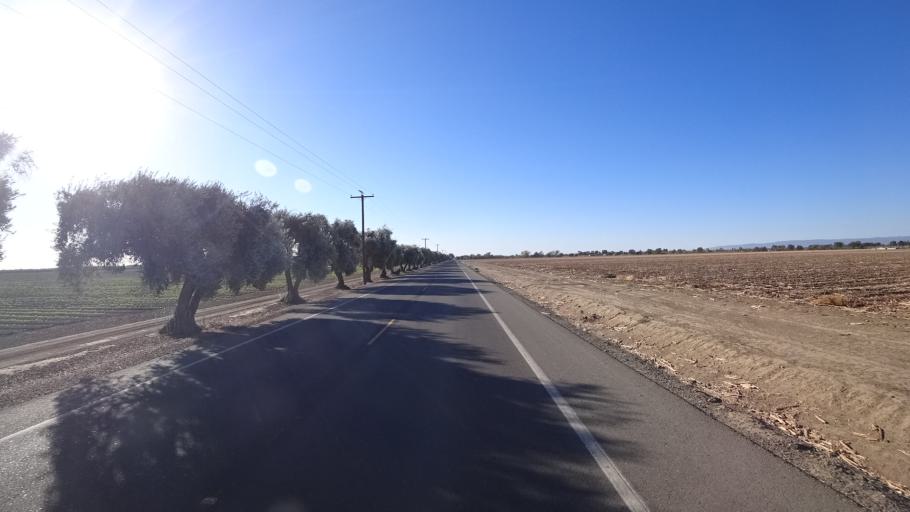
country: US
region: California
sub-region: Yolo County
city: Woodland
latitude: 38.6166
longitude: -121.7851
